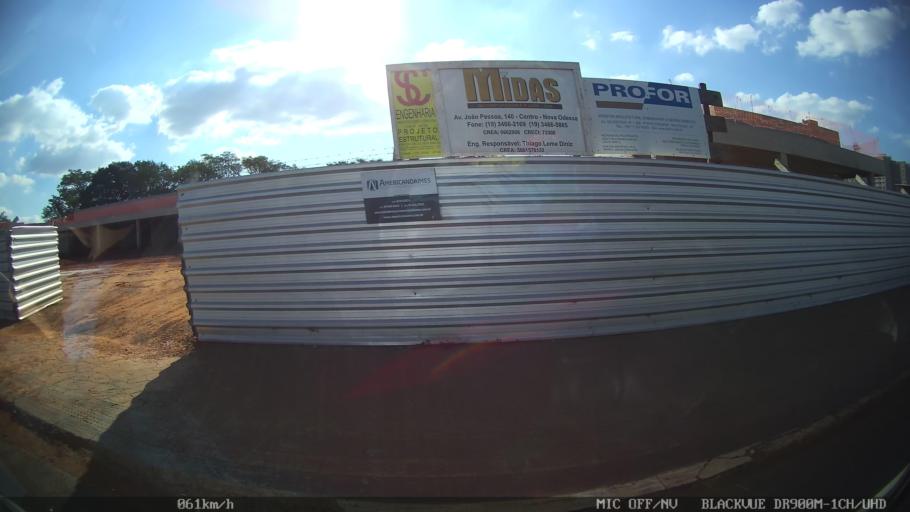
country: BR
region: Sao Paulo
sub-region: Nova Odessa
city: Nova Odessa
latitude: -22.7912
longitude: -47.3084
